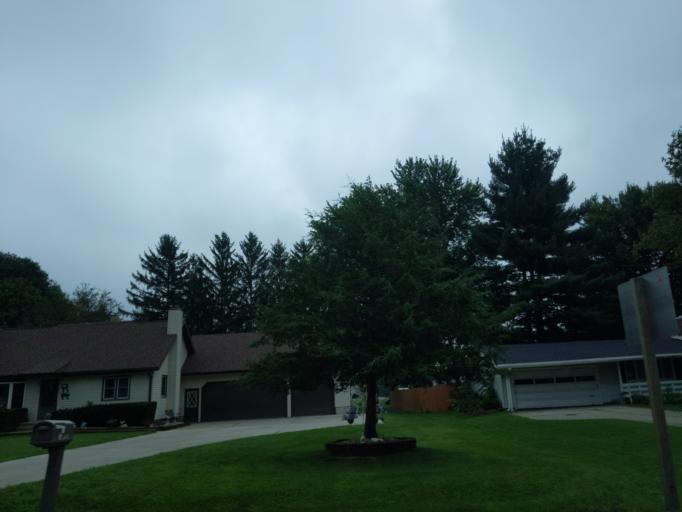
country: US
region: Wisconsin
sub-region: Dane County
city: Black Earth
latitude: 43.1329
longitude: -89.7480
